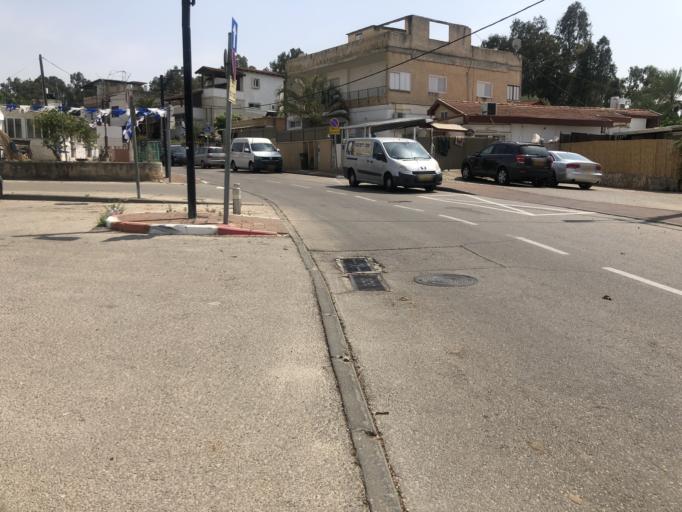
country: IL
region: Central District
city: Rosh Ha'Ayin
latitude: 32.0962
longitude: 34.9389
